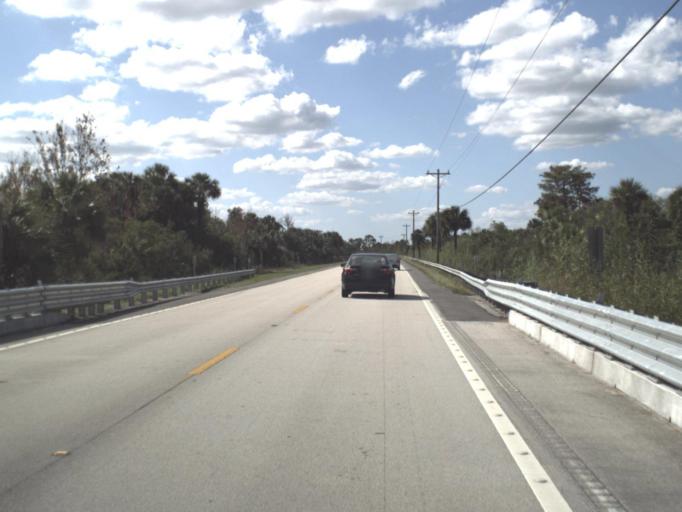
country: US
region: Florida
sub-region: Collier County
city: Marco
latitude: 25.8988
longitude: -81.2881
